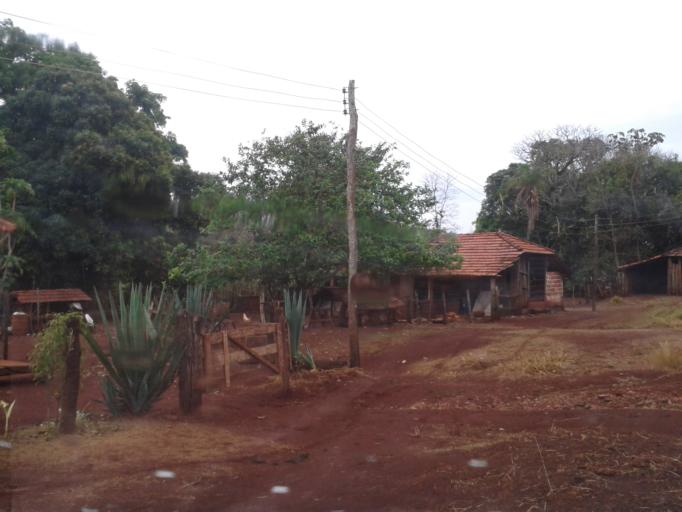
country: BR
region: Minas Gerais
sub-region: Santa Vitoria
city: Santa Vitoria
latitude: -18.8505
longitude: -49.8302
